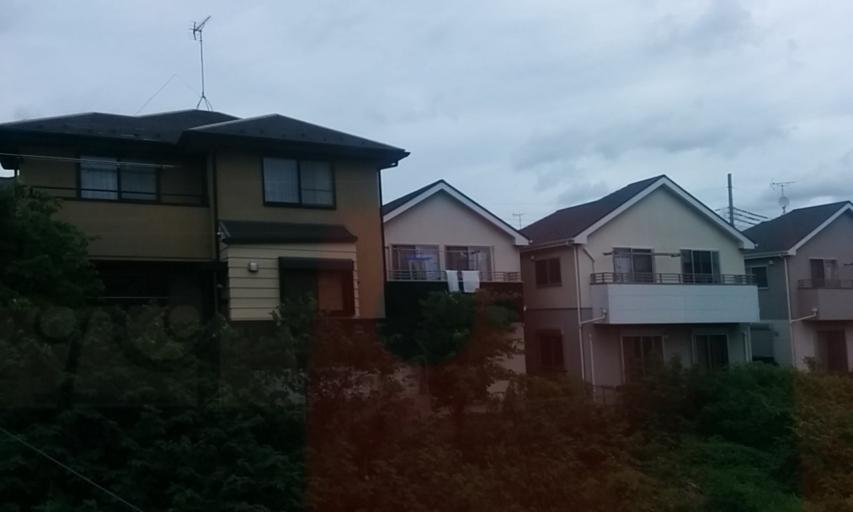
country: JP
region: Tokyo
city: Tanashicho
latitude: 35.7498
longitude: 139.5501
